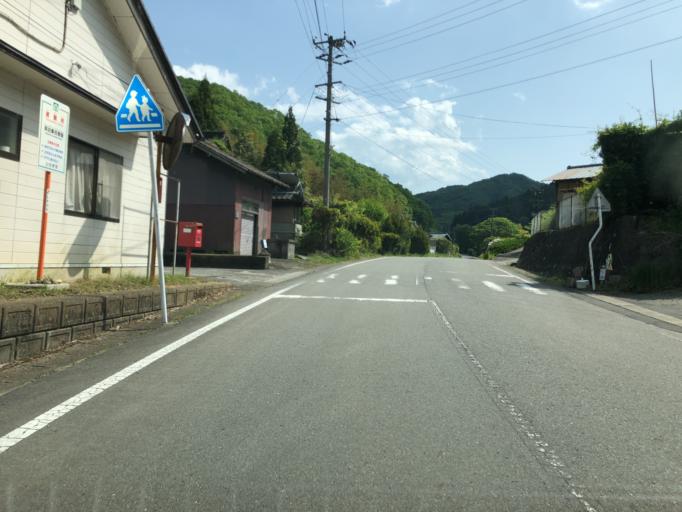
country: JP
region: Fukushima
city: Ishikawa
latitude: 36.9917
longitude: 140.6180
